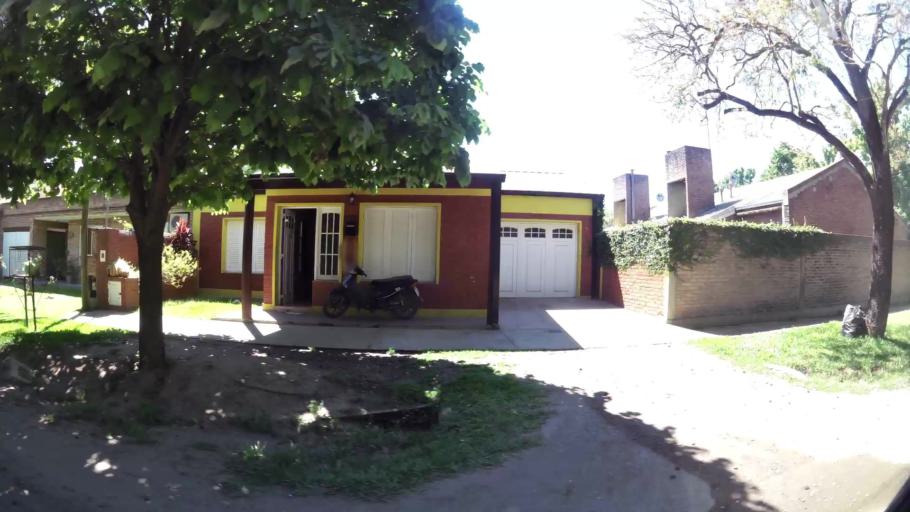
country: AR
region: Santa Fe
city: Esperanza
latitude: -31.4353
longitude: -60.9291
